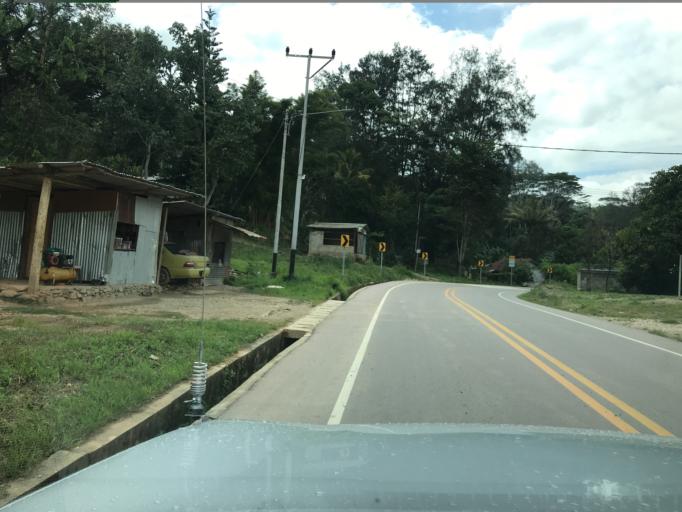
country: TL
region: Aileu
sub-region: Aileu Villa
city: Aileu
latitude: -8.7229
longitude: 125.5641
